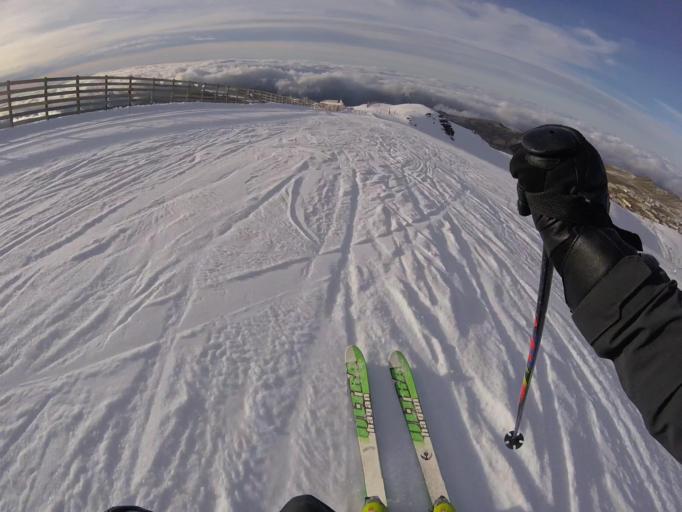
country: ES
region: Andalusia
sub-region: Provincia de Granada
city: Guejar-Sierra
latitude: 37.0695
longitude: -3.3967
